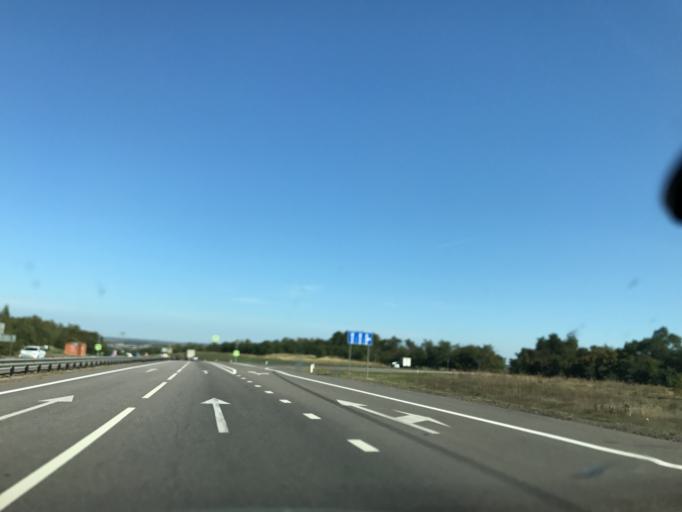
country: RU
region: Voronezj
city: Verkhniy Mamon
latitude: 50.1361
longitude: 40.4346
